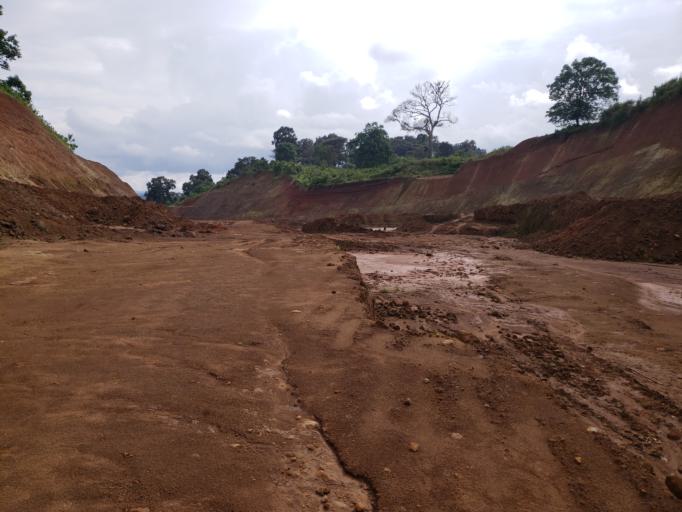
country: ET
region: Oromiya
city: Dodola
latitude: 6.5479
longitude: 39.4222
